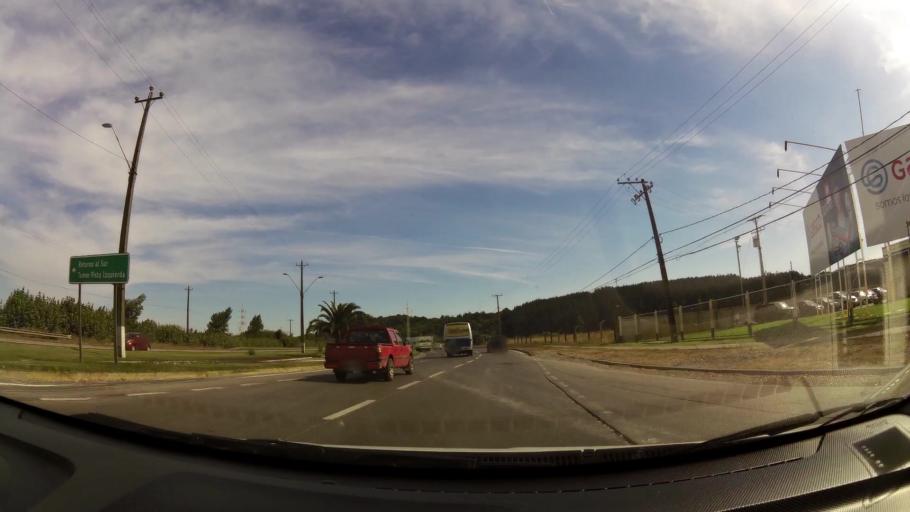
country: CL
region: Biobio
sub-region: Provincia de Concepcion
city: Talcahuano
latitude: -36.7635
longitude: -73.1175
